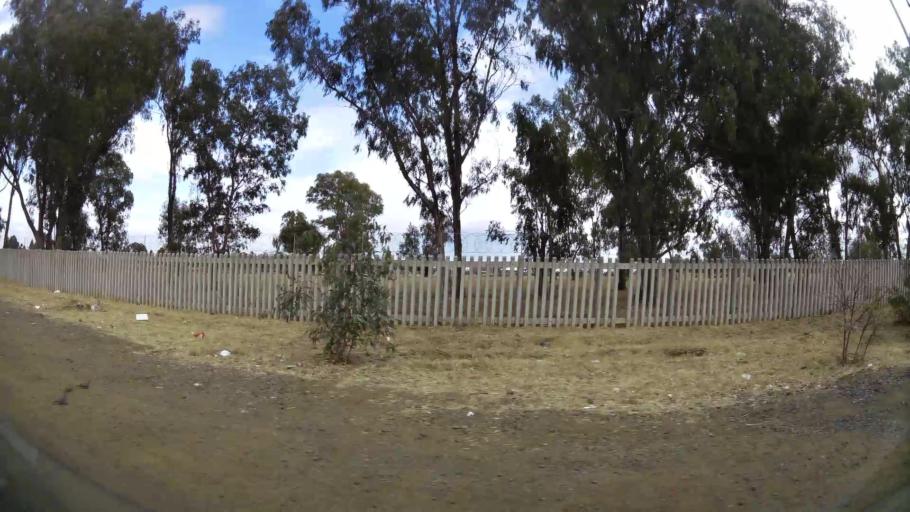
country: ZA
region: Orange Free State
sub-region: Fezile Dabi District Municipality
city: Kroonstad
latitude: -27.6401
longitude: 27.2203
